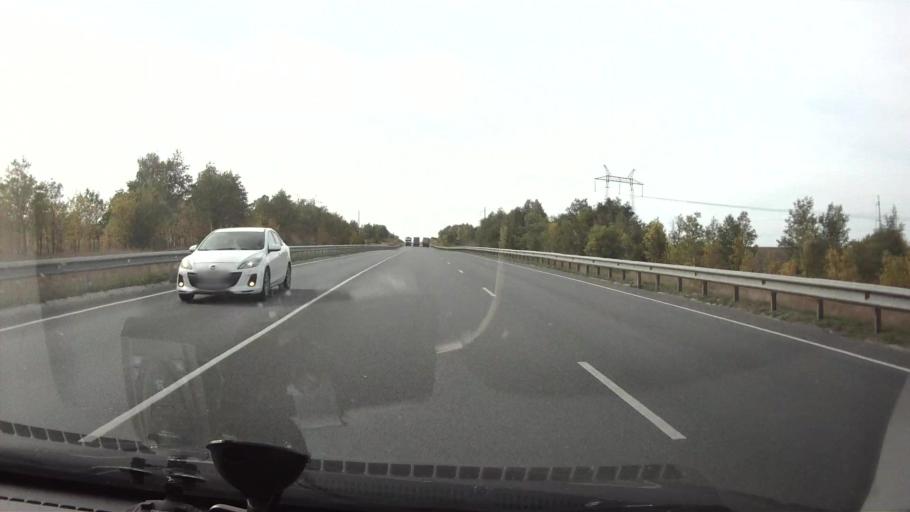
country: RU
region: Saratov
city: Tersa
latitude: 52.1001
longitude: 47.5171
